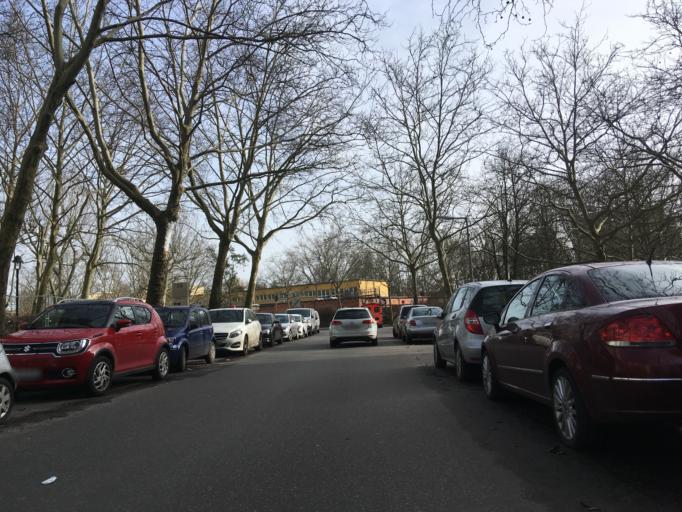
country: DE
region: Berlin
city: Markisches Viertel
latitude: 52.6013
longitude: 13.3618
